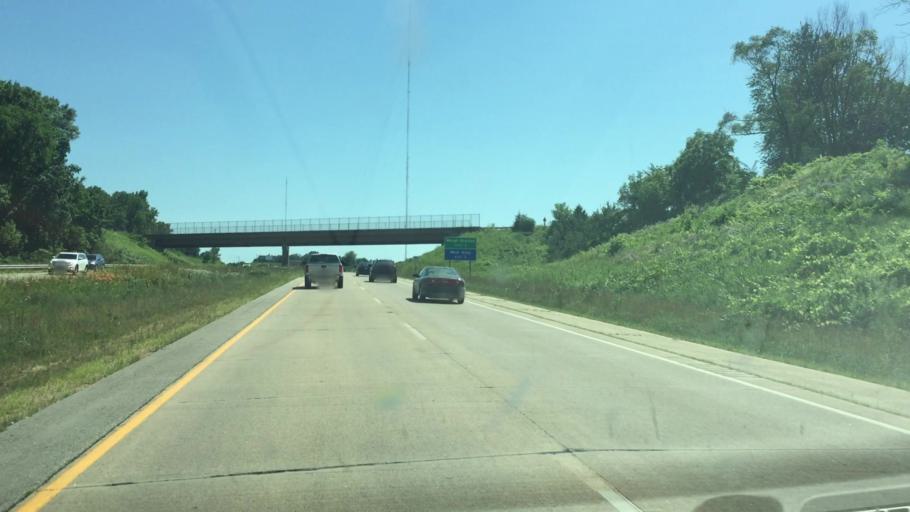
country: US
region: Illinois
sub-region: Jo Daviess County
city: East Dubuque
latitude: 42.5369
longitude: -90.6105
